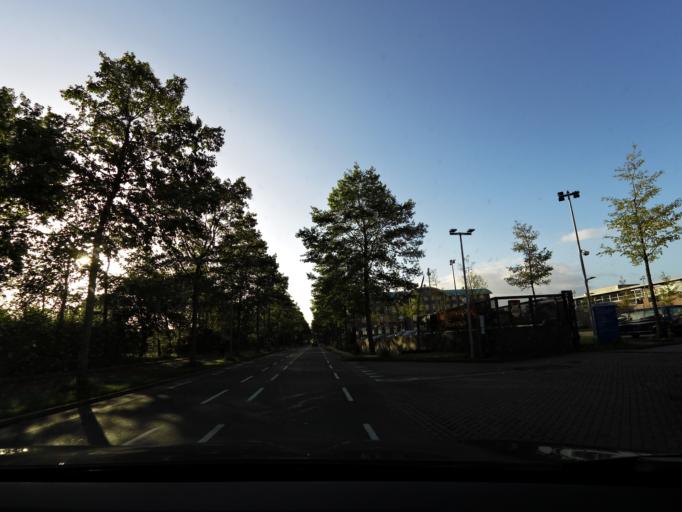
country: NL
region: South Holland
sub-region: Gemeente Rotterdam
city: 's-Gravenland
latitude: 51.9096
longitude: 4.5273
